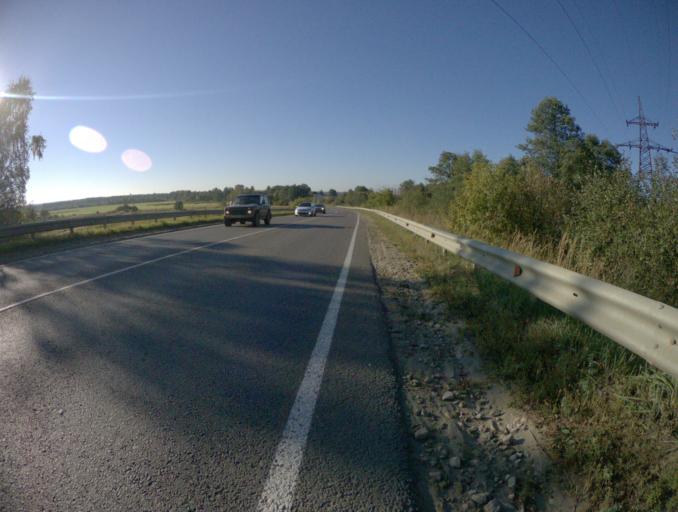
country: RU
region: Vladimir
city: Sobinka
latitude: 56.0182
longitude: 39.9927
